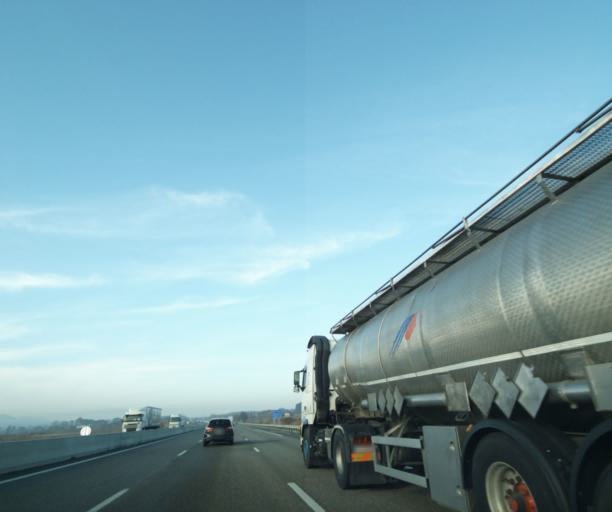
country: FR
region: Provence-Alpes-Cote d'Azur
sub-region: Departement des Bouches-du-Rhone
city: Trets
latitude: 43.4707
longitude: 5.6736
